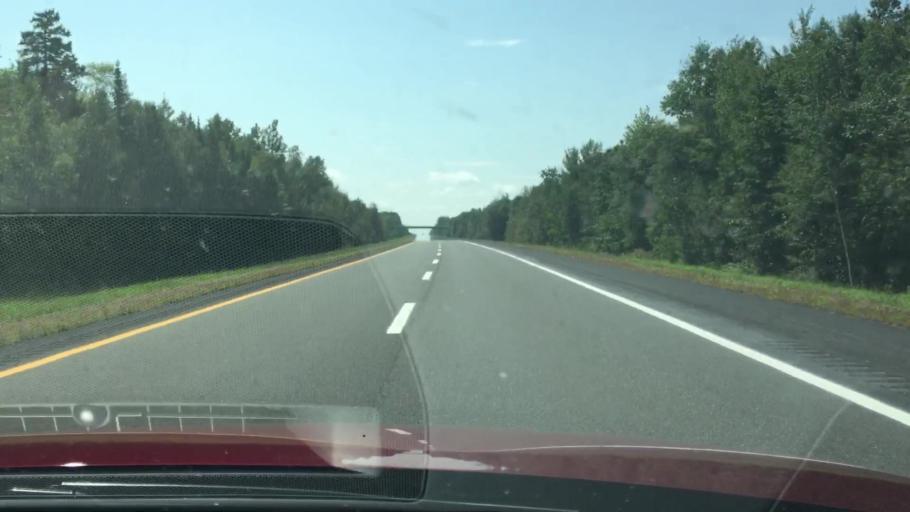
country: US
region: Maine
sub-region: Penobscot County
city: Patten
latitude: 45.9522
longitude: -68.3331
